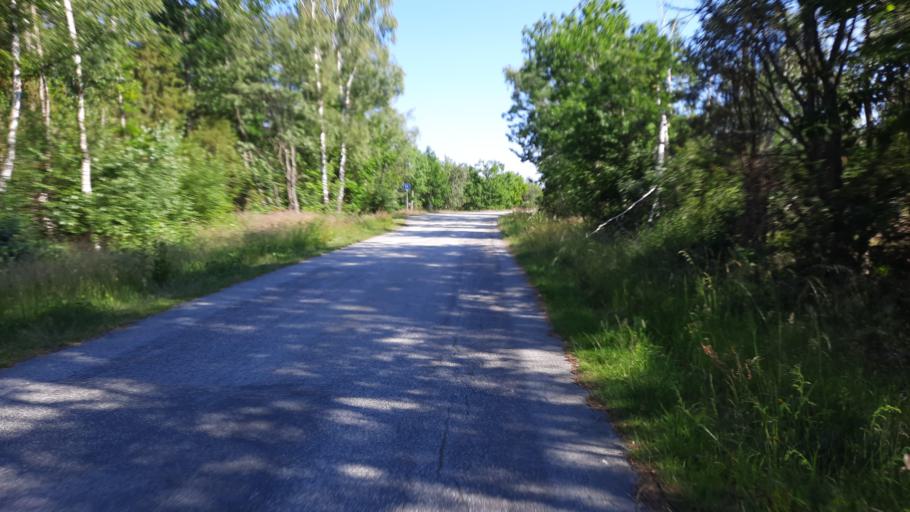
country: SE
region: Blekinge
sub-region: Karlskrona Kommun
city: Sturko
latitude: 56.1231
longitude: 15.6592
